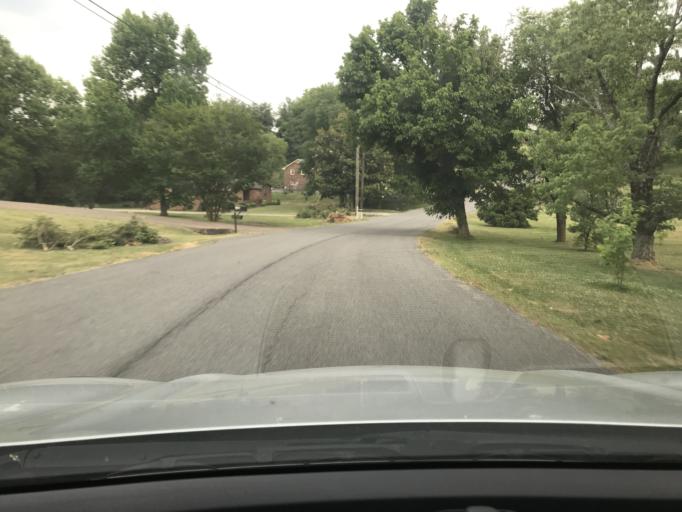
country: US
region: Tennessee
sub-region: Davidson County
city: Goodlettsville
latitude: 36.3036
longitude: -86.7118
